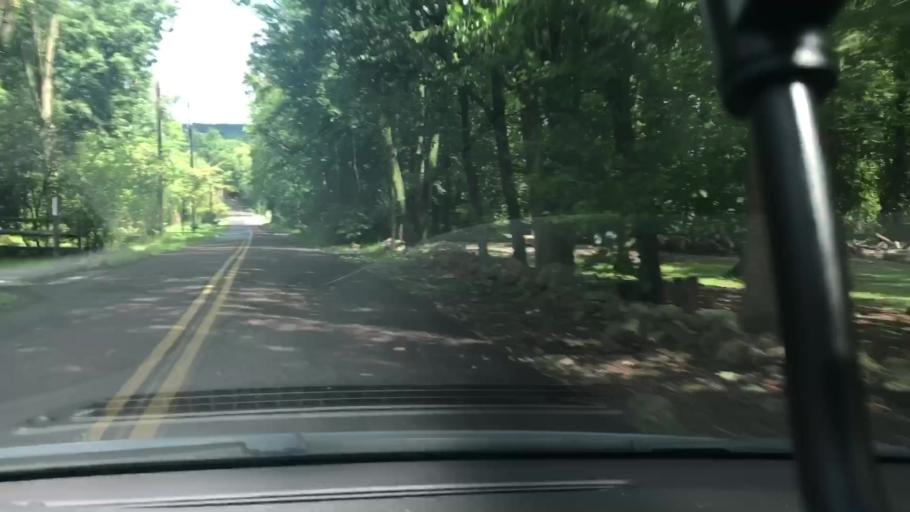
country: US
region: Pennsylvania
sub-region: Chester County
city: Kenilworth
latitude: 40.1823
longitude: -75.6509
